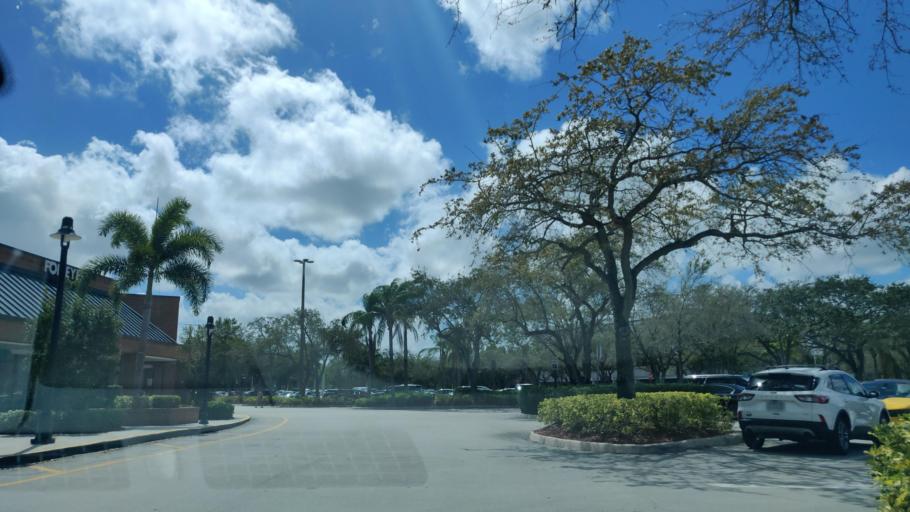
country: US
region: Florida
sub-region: Broward County
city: Weston
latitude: 26.1045
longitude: -80.3636
